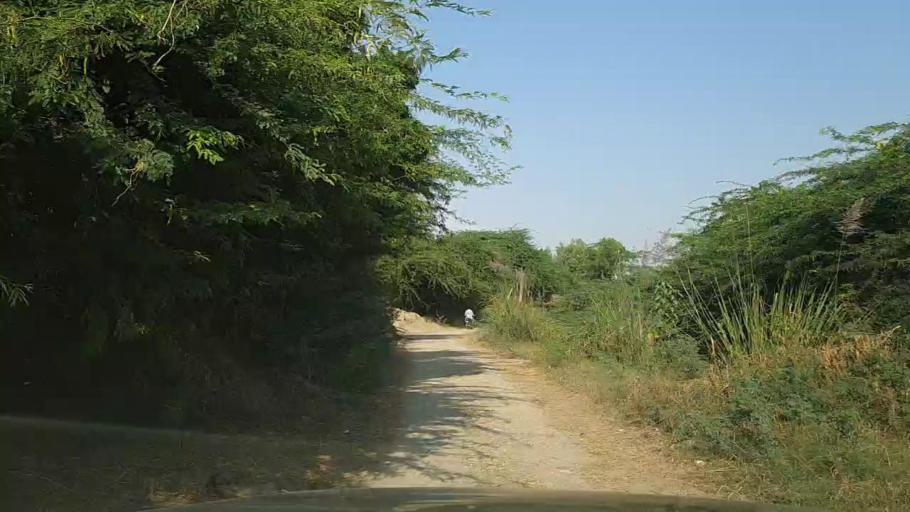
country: PK
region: Sindh
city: Thatta
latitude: 24.7970
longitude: 67.8232
